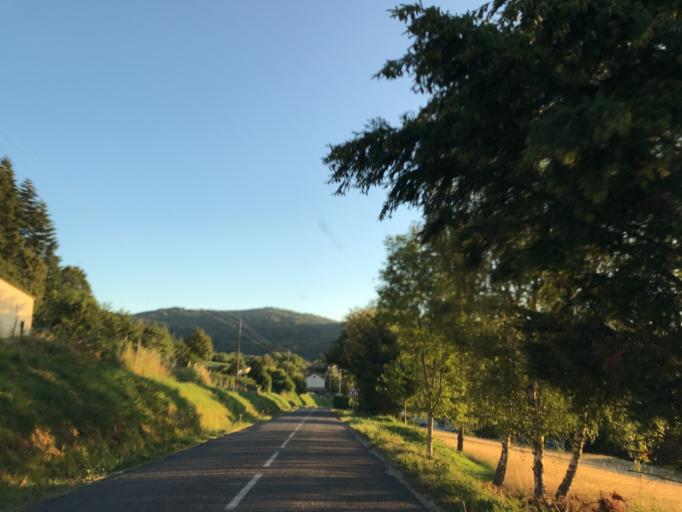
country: FR
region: Auvergne
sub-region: Departement du Puy-de-Dome
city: Chabreloche
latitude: 45.8279
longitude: 3.6826
